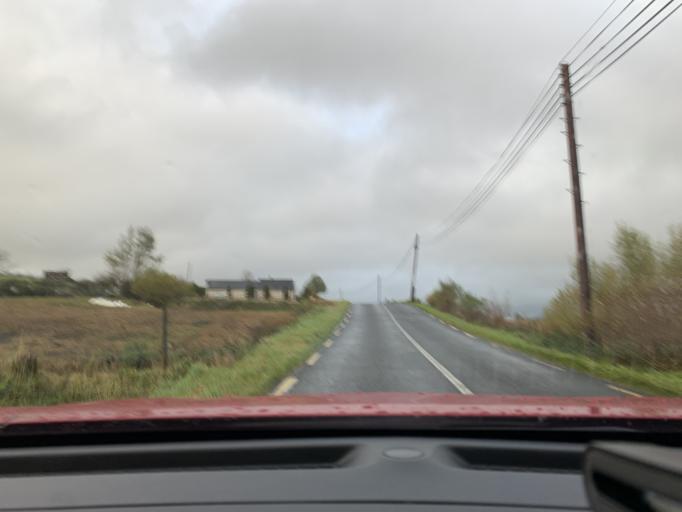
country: IE
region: Connaught
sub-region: Sligo
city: Ballymote
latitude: 54.0144
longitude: -8.5223
